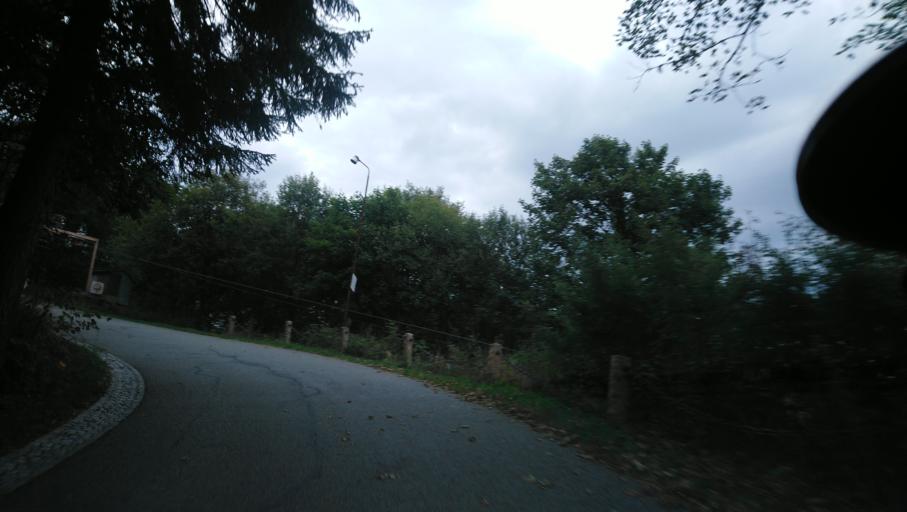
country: DE
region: Saxony
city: Barenstein
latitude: 50.5070
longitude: 13.0222
